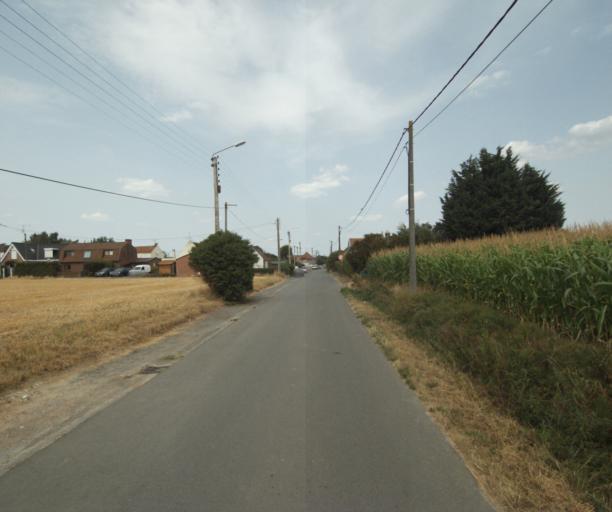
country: BE
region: Wallonia
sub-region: Province du Hainaut
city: Estaimpuis
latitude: 50.6993
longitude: 3.2604
